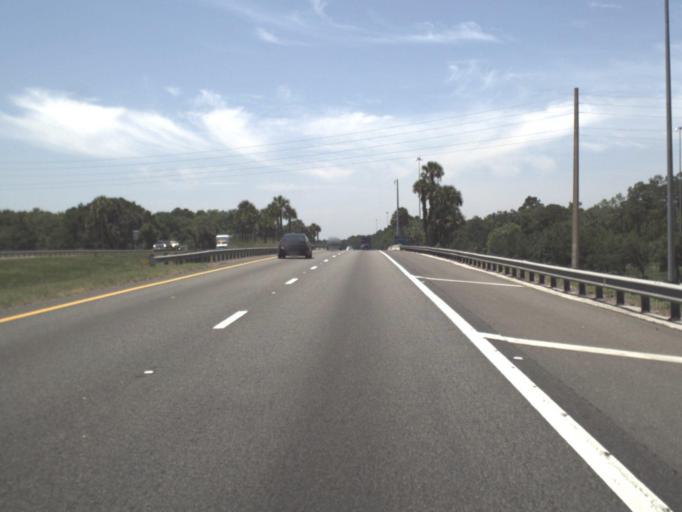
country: US
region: Florida
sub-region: Duval County
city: Jacksonville
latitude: 30.4602
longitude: -81.6767
